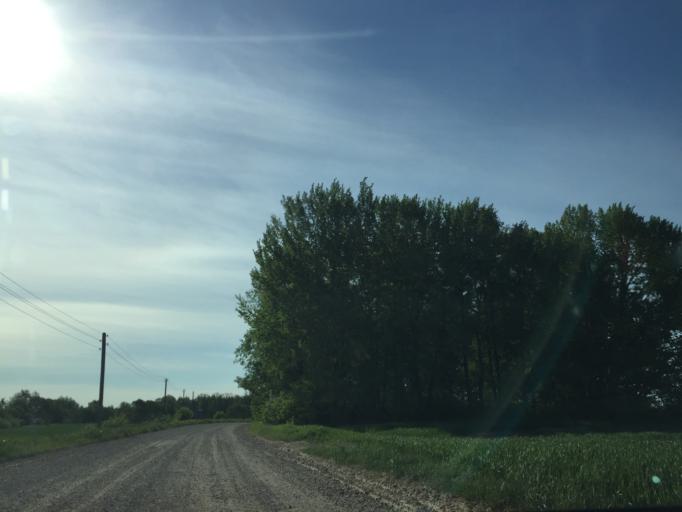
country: LV
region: Bauskas Rajons
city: Bauska
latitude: 56.2860
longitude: 24.3783
